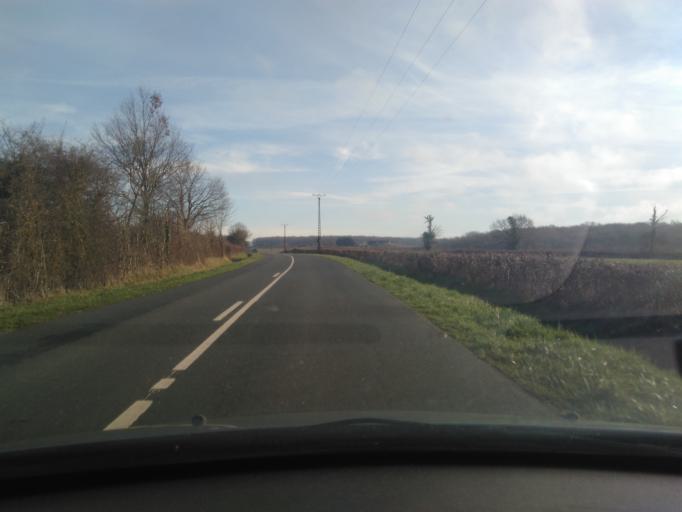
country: FR
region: Centre
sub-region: Departement de l'Indre
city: Montgivray
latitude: 46.6388
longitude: 2.0836
